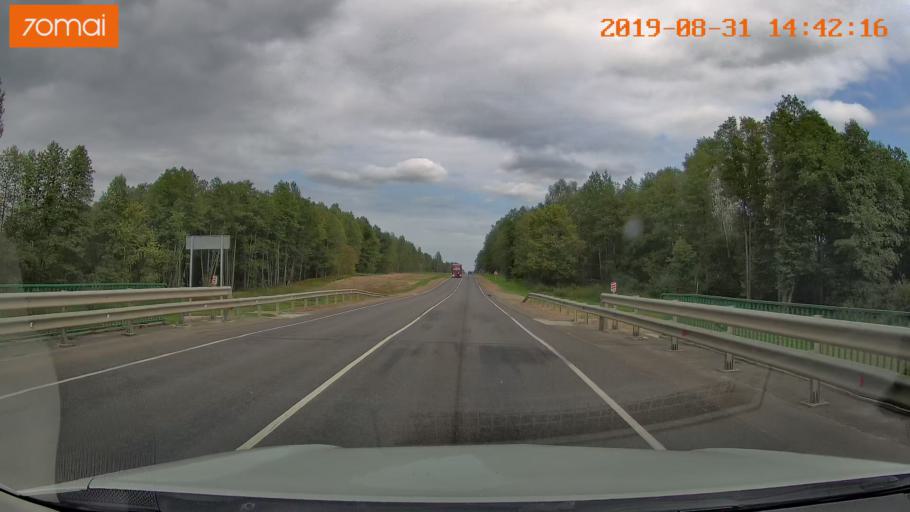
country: RU
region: Smolensk
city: Yekimovichi
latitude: 54.2068
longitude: 33.6046
